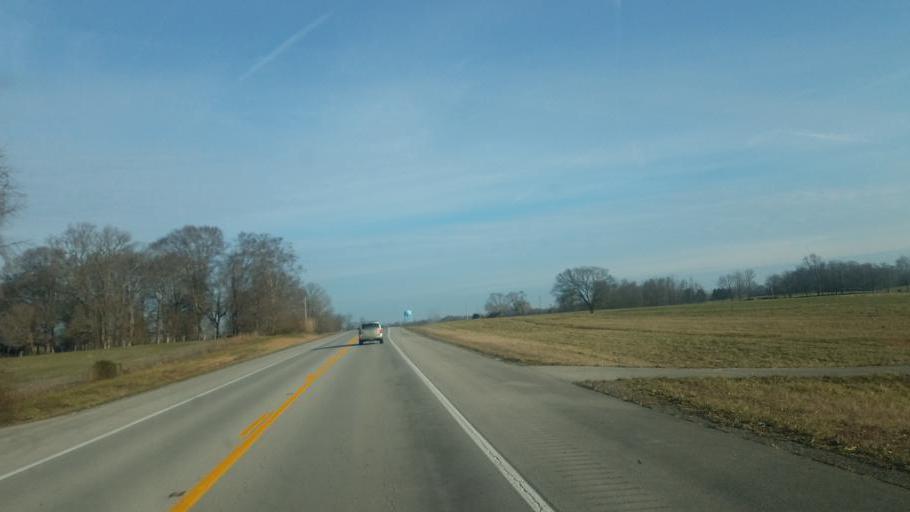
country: US
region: Kentucky
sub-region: Russell County
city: Jamestown
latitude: 36.9886
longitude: -85.0843
